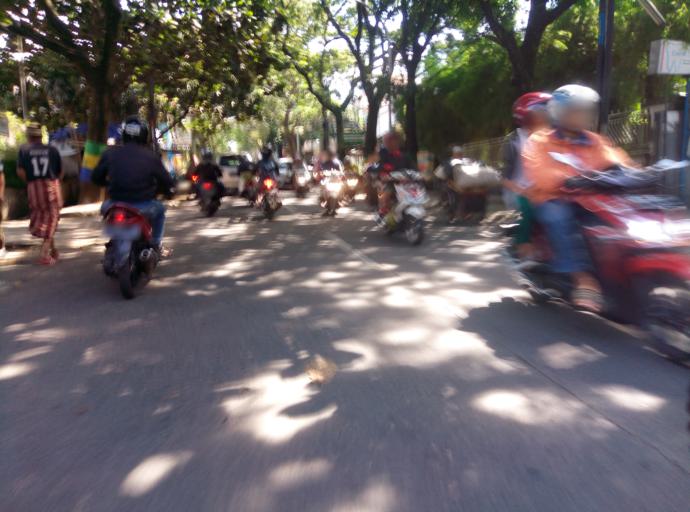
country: ID
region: West Java
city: Bandung
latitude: -6.8851
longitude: 107.6199
